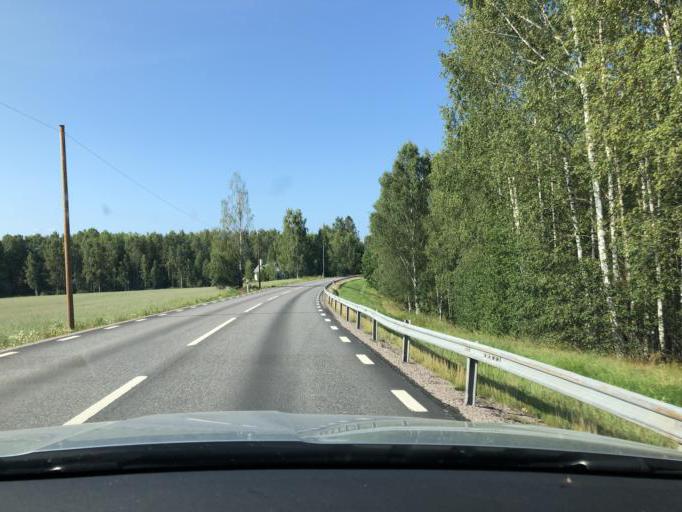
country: SE
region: Dalarna
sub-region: Saters Kommun
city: Saeter
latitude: 60.4144
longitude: 15.8496
